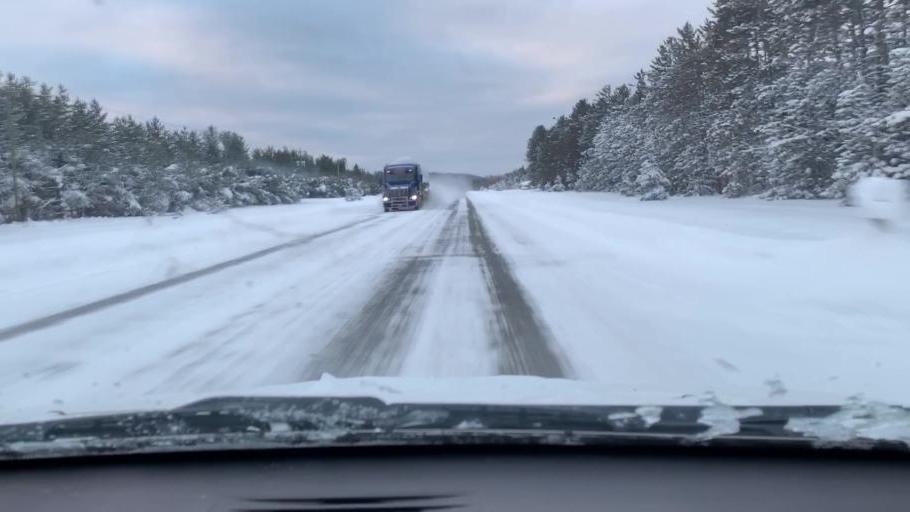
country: US
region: Michigan
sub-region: Antrim County
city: Mancelona
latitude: 44.9231
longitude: -85.0510
